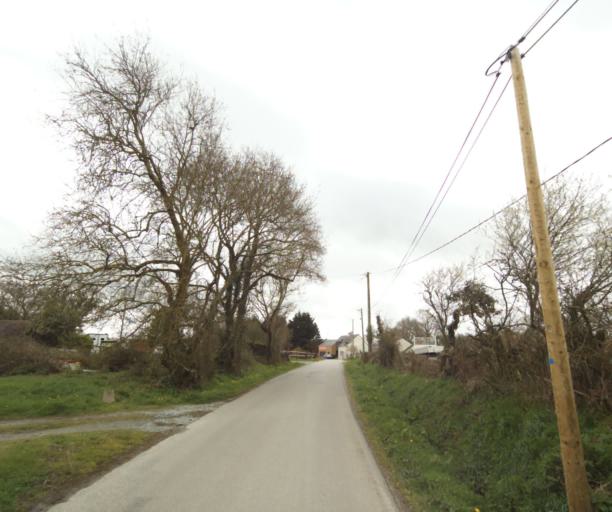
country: FR
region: Pays de la Loire
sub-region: Departement de la Loire-Atlantique
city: Bouvron
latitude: 47.4319
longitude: -1.8573
